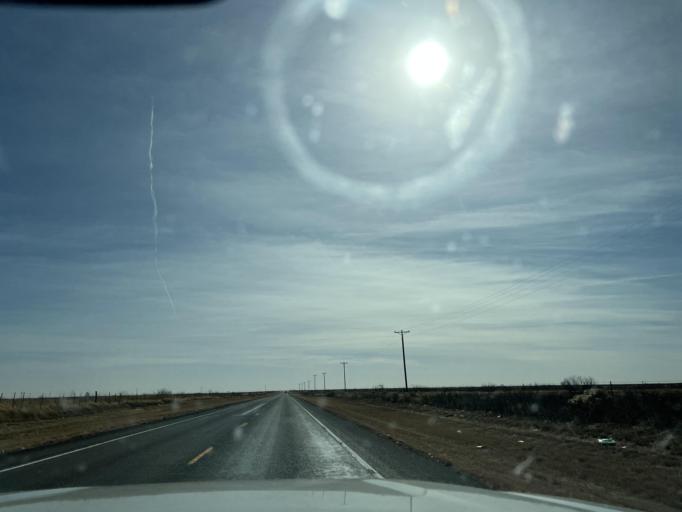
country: US
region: Texas
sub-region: Andrews County
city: Andrews
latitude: 32.4129
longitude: -102.4307
